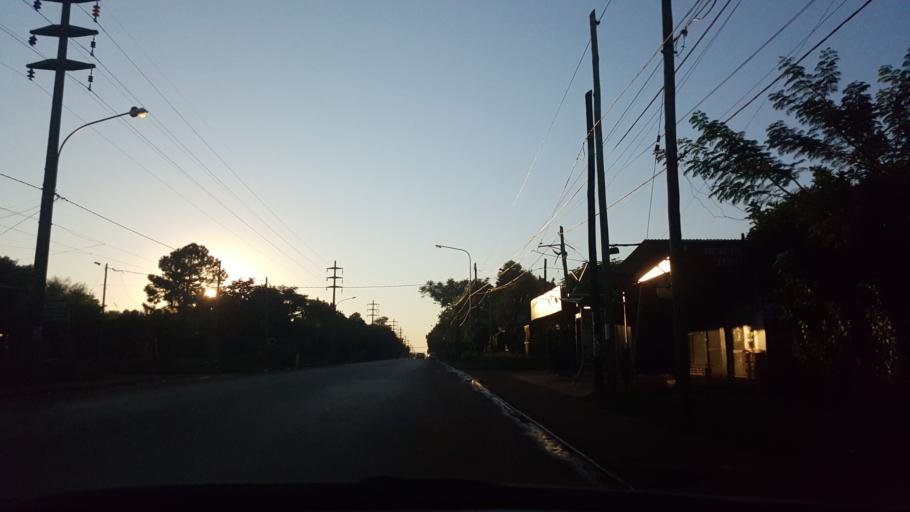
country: AR
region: Misiones
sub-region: Departamento de Capital
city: Posadas
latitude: -27.3724
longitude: -55.9461
